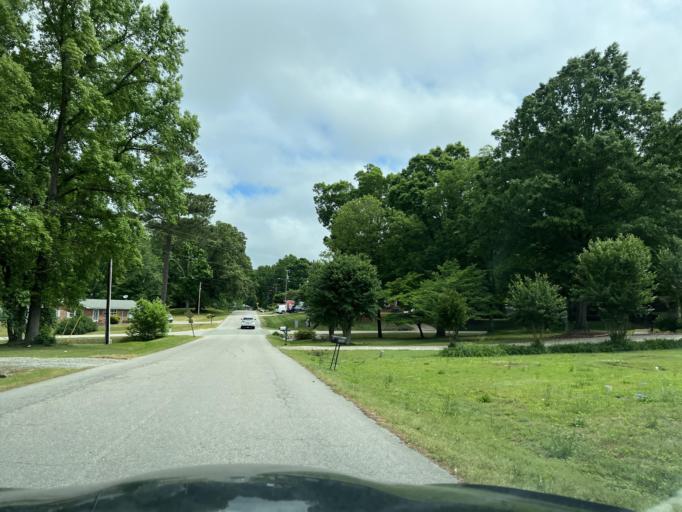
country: US
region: North Carolina
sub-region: Wake County
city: Rolesville
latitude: 35.8734
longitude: -78.5455
